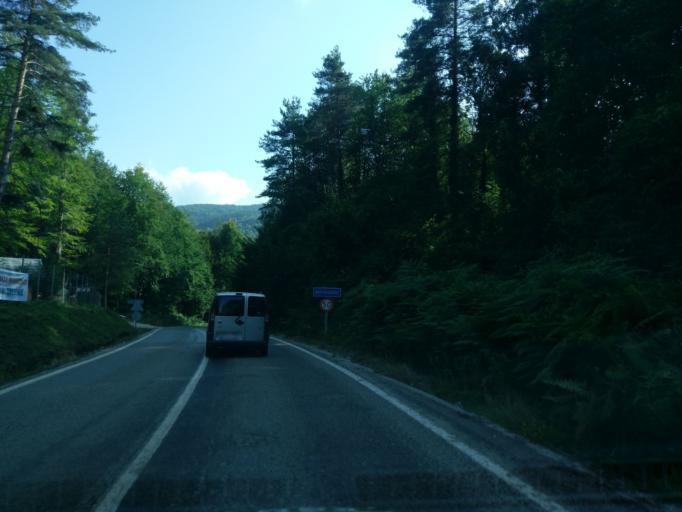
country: TR
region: Sinop
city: Ayancik
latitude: 41.8815
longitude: 34.5137
